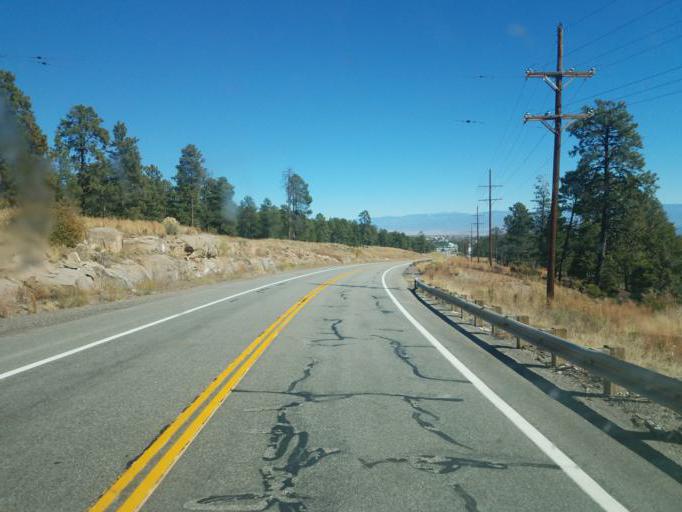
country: US
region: New Mexico
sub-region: Los Alamos County
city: Los Alamos
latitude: 35.8741
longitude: -106.3409
